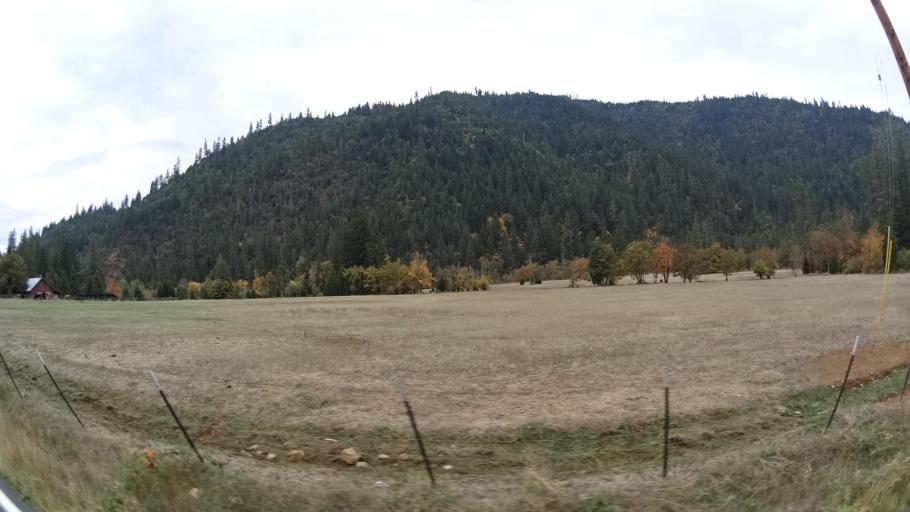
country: US
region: California
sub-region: Siskiyou County
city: Happy Camp
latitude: 41.8756
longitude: -123.4147
